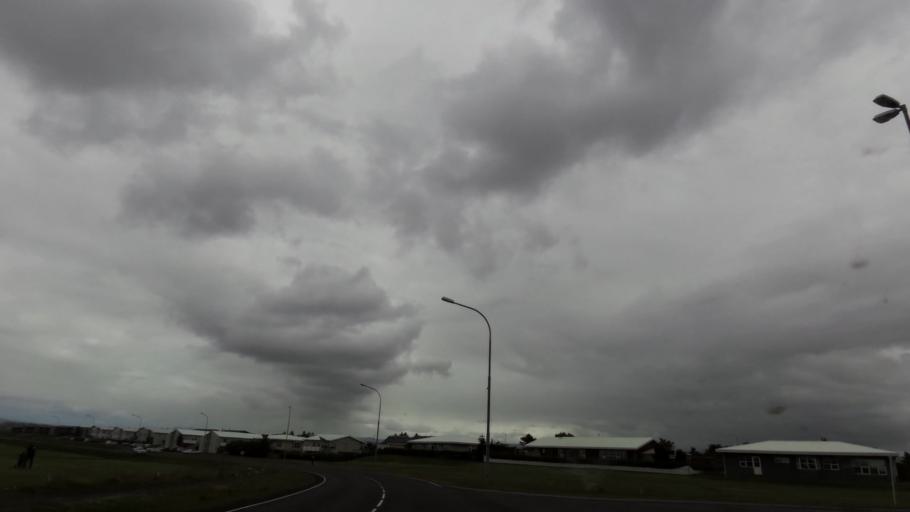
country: IS
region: Capital Region
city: Alftanes
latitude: 64.1000
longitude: -22.0252
